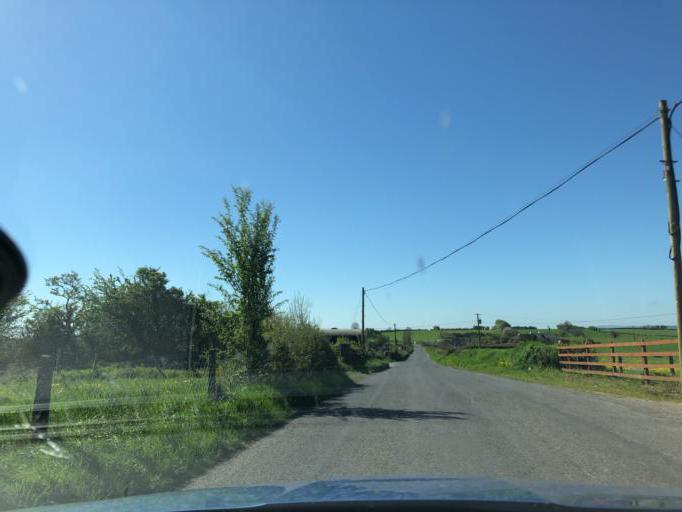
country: IE
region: Connaught
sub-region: County Galway
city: Portumna
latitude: 53.1609
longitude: -8.2944
